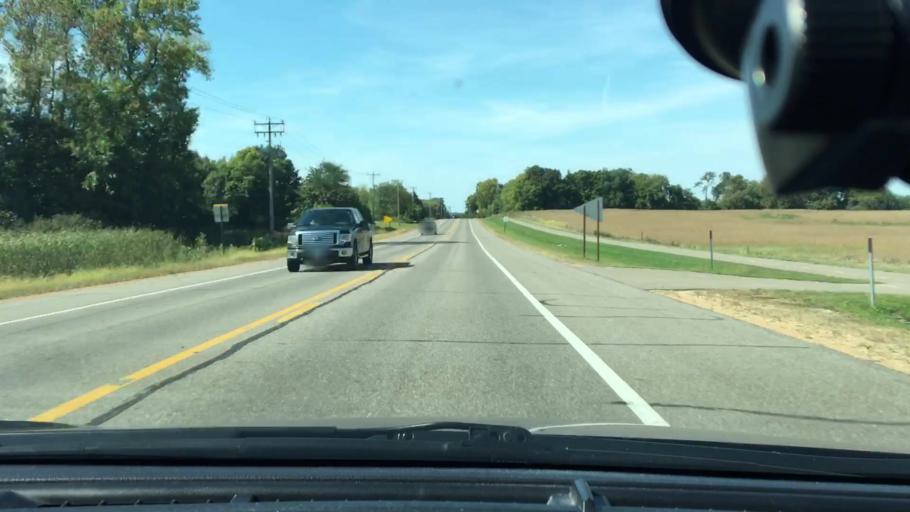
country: US
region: Minnesota
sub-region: Wright County
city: Hanover
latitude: 45.1525
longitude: -93.6517
